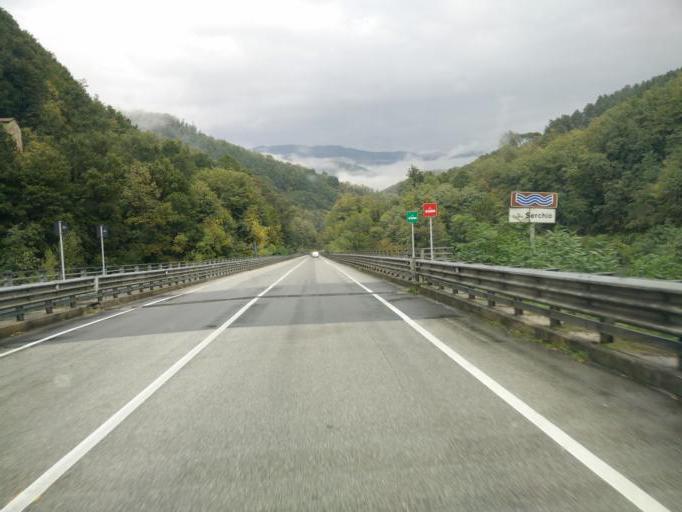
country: IT
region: Tuscany
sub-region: Provincia di Lucca
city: Castelnuovo di Garfagnana
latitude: 44.1146
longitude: 10.4209
